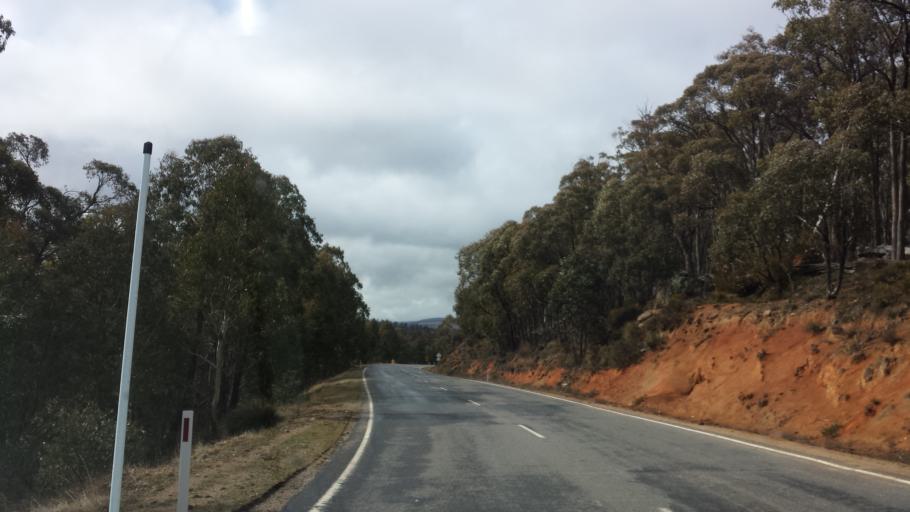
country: AU
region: Victoria
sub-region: Alpine
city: Mount Beauty
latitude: -37.0828
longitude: 147.3762
